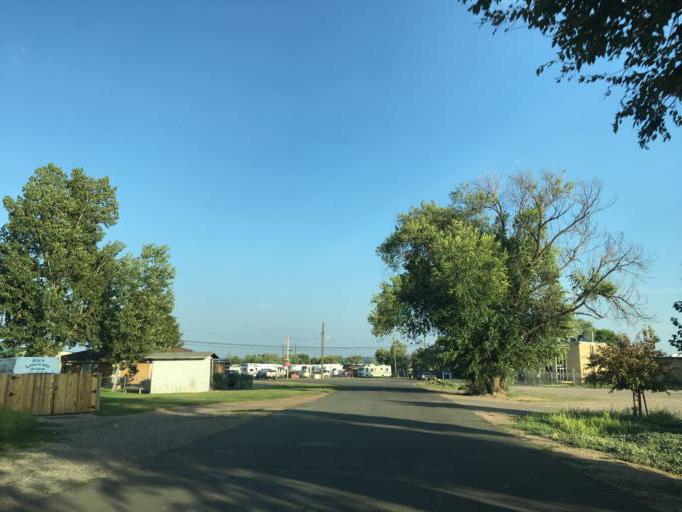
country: US
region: Colorado
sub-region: Jefferson County
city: Applewood
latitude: 39.7817
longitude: -105.1666
